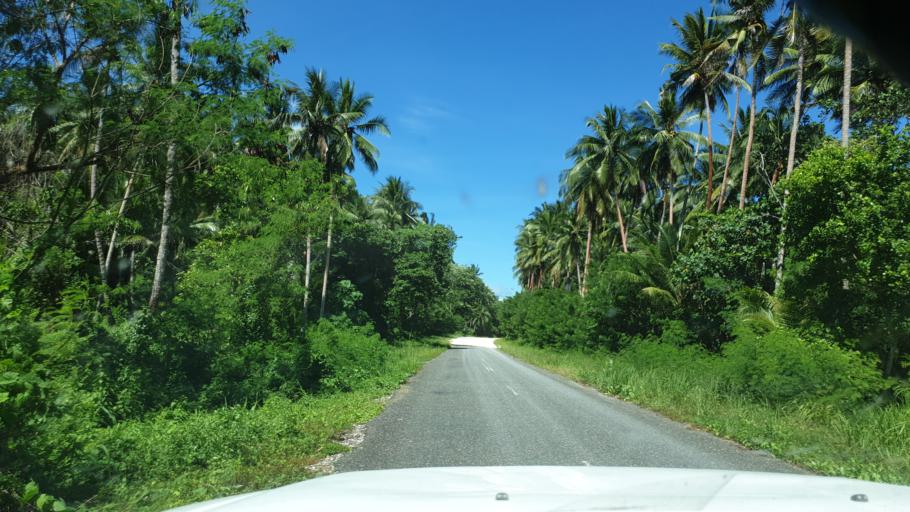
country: PG
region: Madang
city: Madang
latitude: -4.4629
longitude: 145.4070
